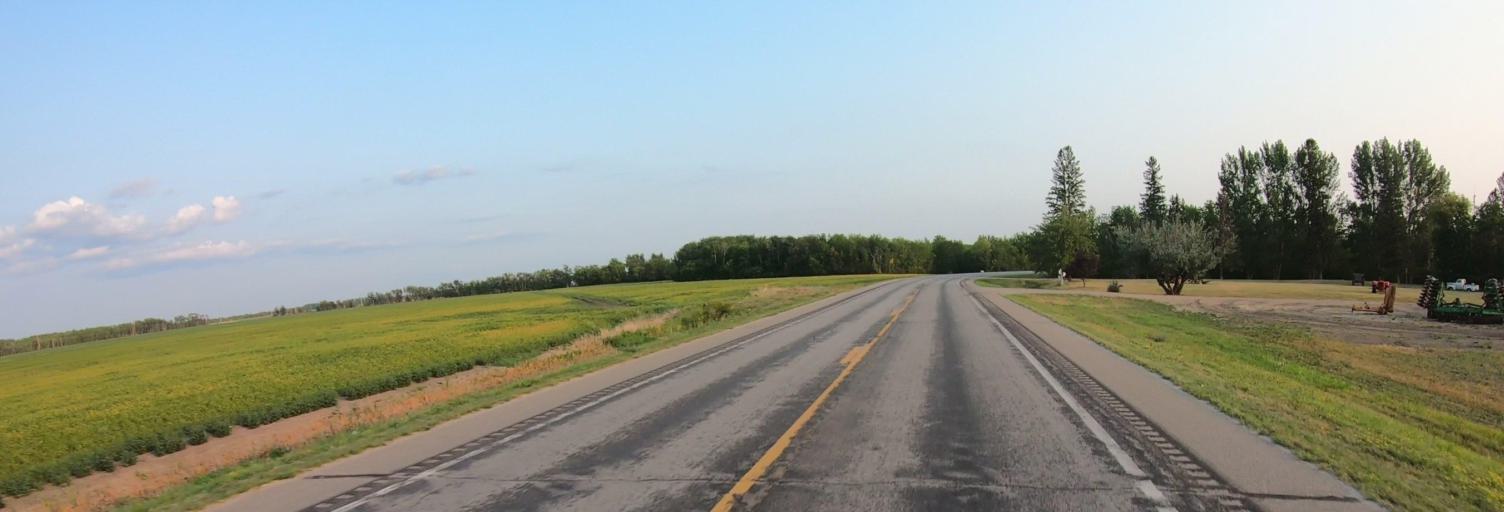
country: US
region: Minnesota
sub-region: Roseau County
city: Warroad
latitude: 48.8835
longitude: -95.3194
